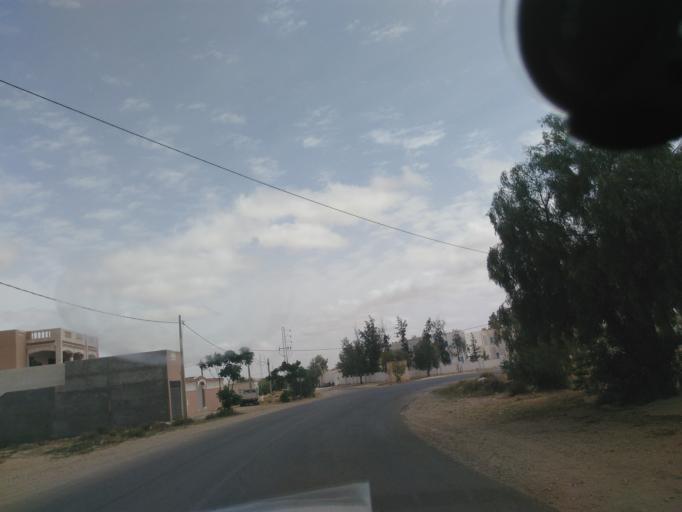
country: TN
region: Tataouine
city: Tataouine
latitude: 32.9554
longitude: 10.4653
